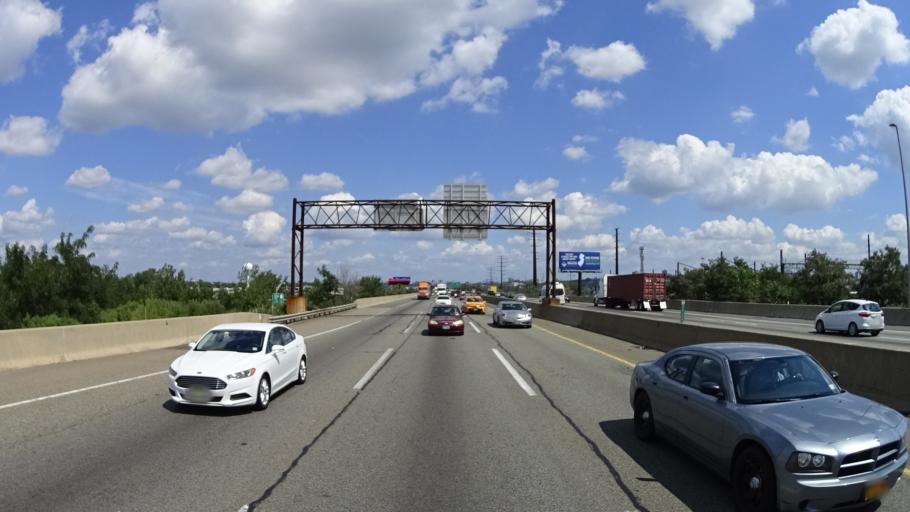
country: US
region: New Jersey
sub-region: Hudson County
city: Secaucus
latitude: 40.7631
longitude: -74.0741
